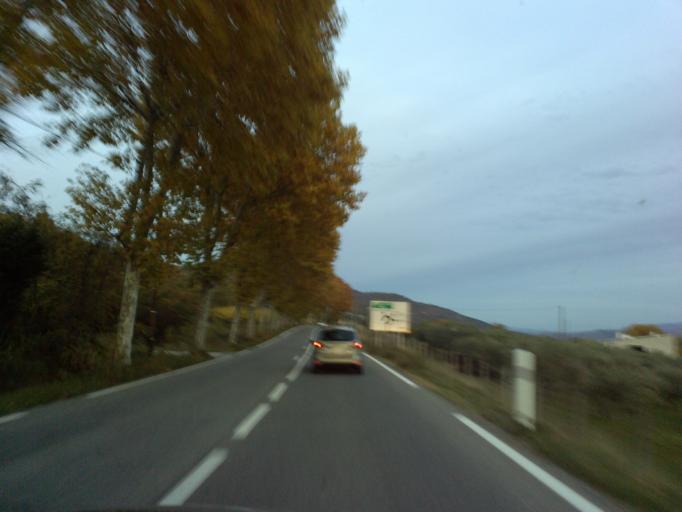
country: FR
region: Provence-Alpes-Cote d'Azur
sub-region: Departement des Alpes-de-Haute-Provence
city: Malijai
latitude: 44.0461
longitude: 6.0412
